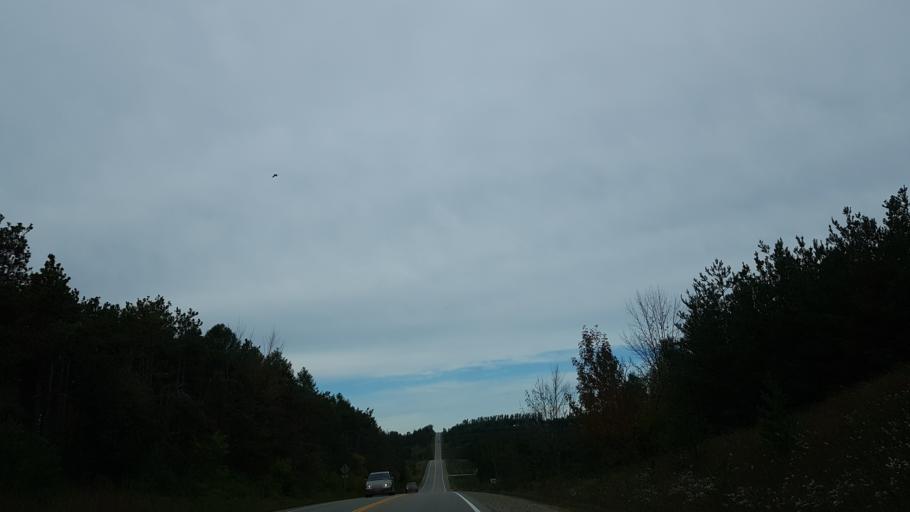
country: CA
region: Ontario
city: Orangeville
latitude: 44.0818
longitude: -80.0190
